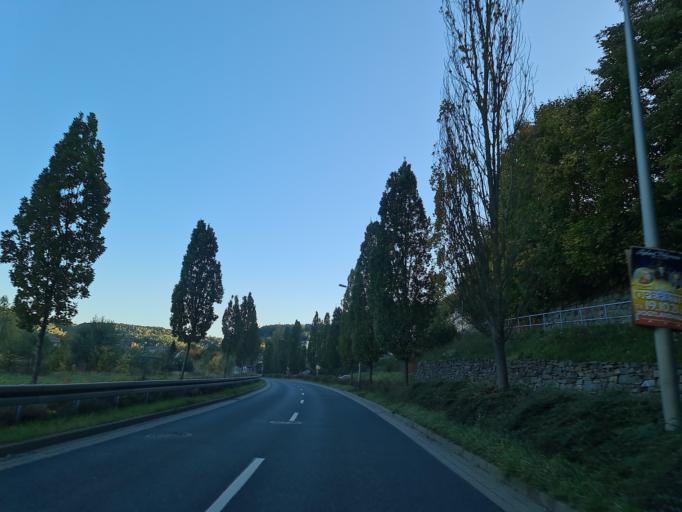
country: DE
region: Thuringia
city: Greiz
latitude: 50.6518
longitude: 12.1932
